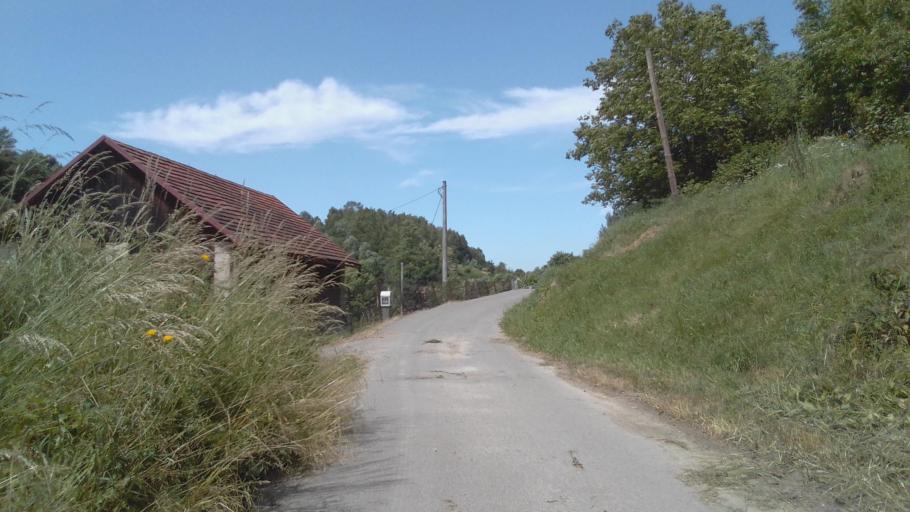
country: PL
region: Subcarpathian Voivodeship
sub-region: Powiat strzyzowski
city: Strzyzow
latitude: 49.8608
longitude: 21.8363
